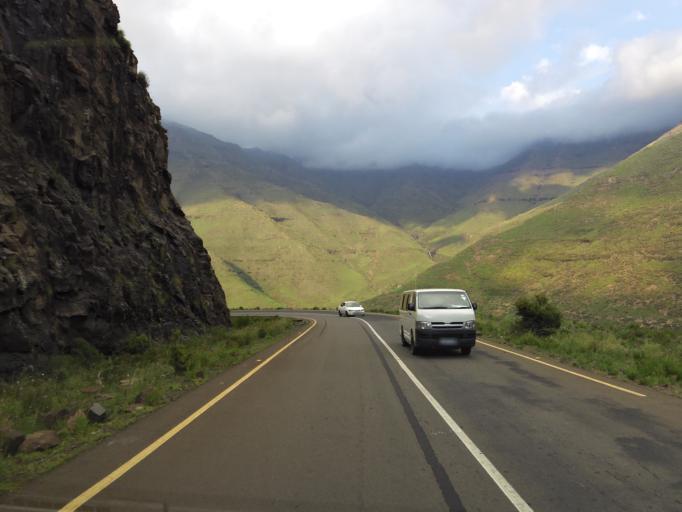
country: LS
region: Butha-Buthe
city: Butha-Buthe
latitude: -29.0650
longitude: 28.3708
